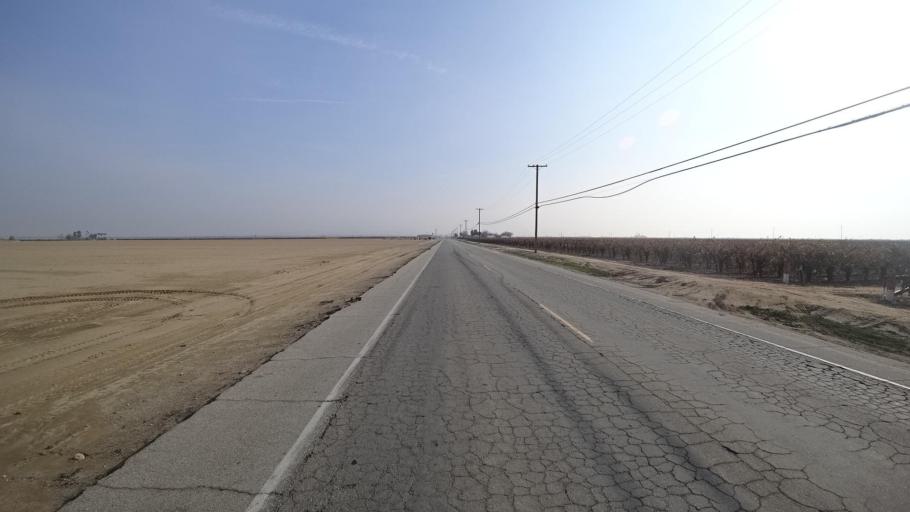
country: US
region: California
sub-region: Kern County
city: Weedpatch
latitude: 35.0930
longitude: -118.9229
